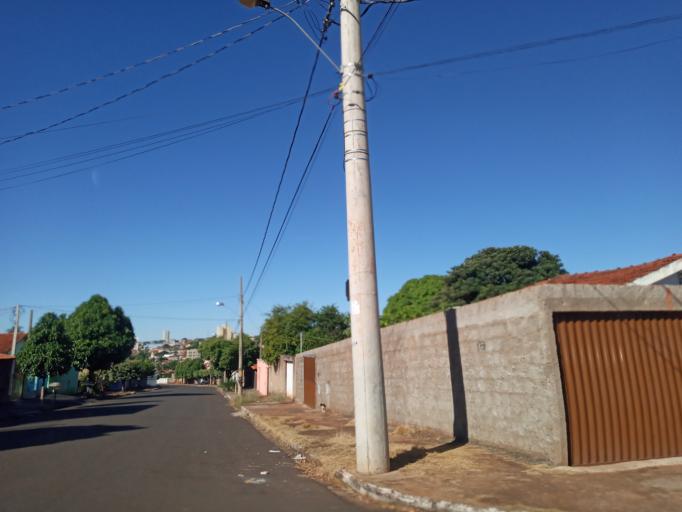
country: BR
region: Minas Gerais
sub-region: Ituiutaba
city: Ituiutaba
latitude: -18.9799
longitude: -49.4760
